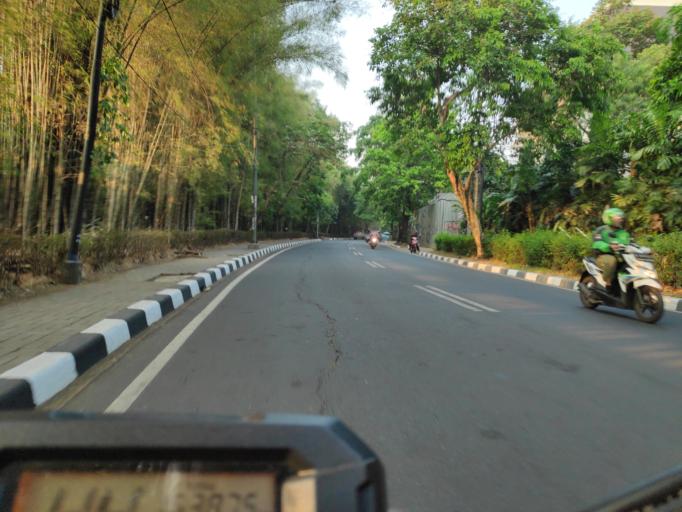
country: ID
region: Jakarta Raya
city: Jakarta
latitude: -6.2506
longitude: 106.8037
